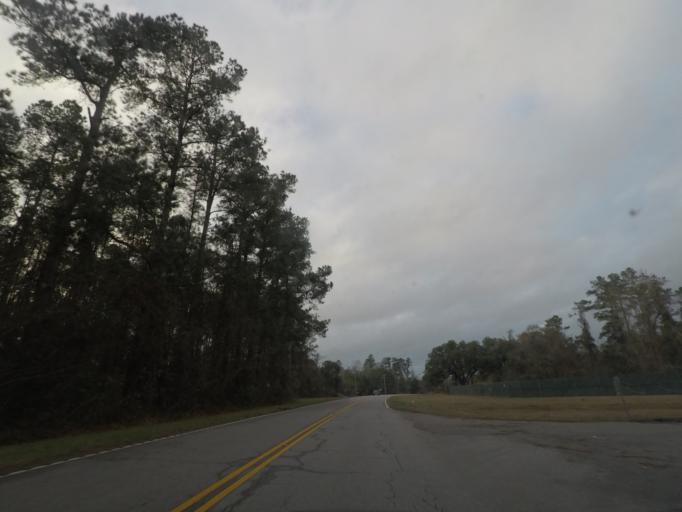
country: US
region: South Carolina
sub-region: Dorchester County
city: Saint George
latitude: 33.0611
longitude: -80.6285
